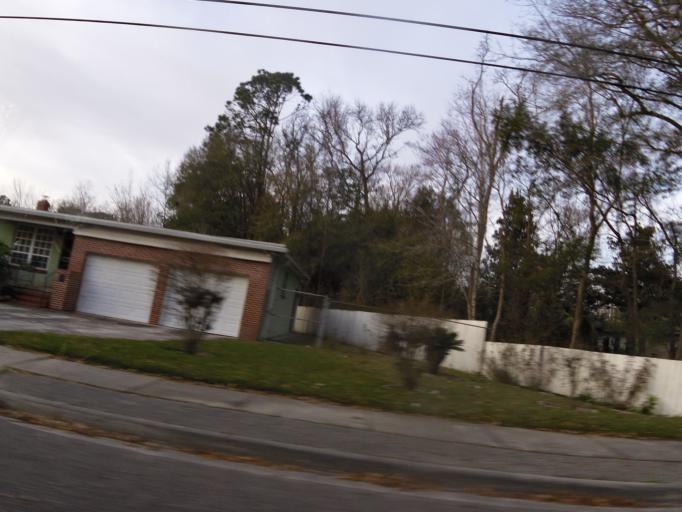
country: US
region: Florida
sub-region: Duval County
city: Jacksonville
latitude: 30.3715
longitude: -81.7025
